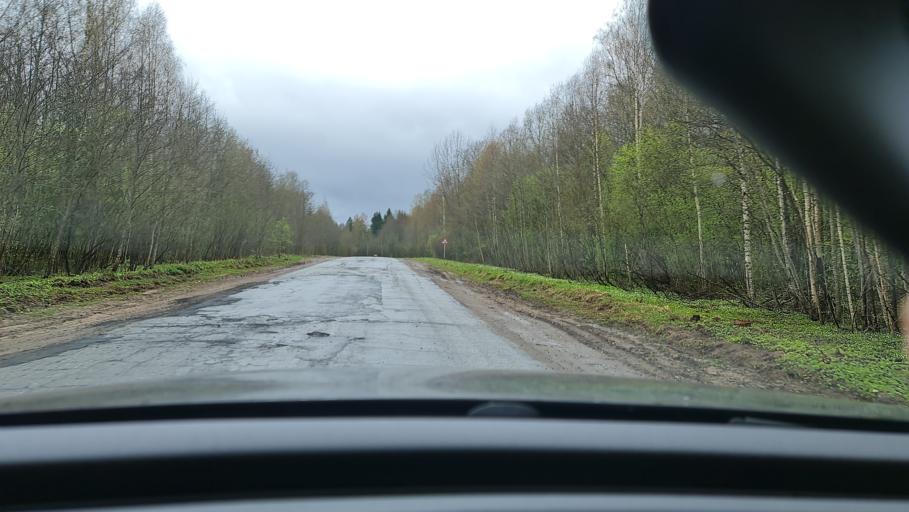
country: RU
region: Novgorod
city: Marevo
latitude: 57.2946
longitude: 32.0835
